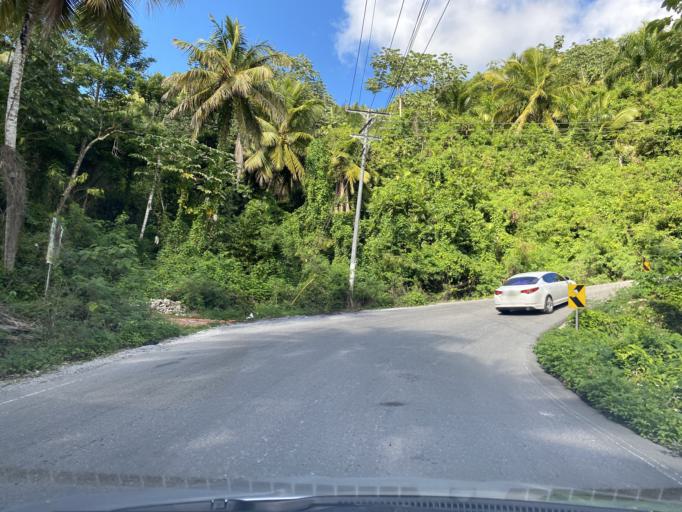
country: DO
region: Samana
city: Sanchez
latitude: 19.2347
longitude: -69.5984
